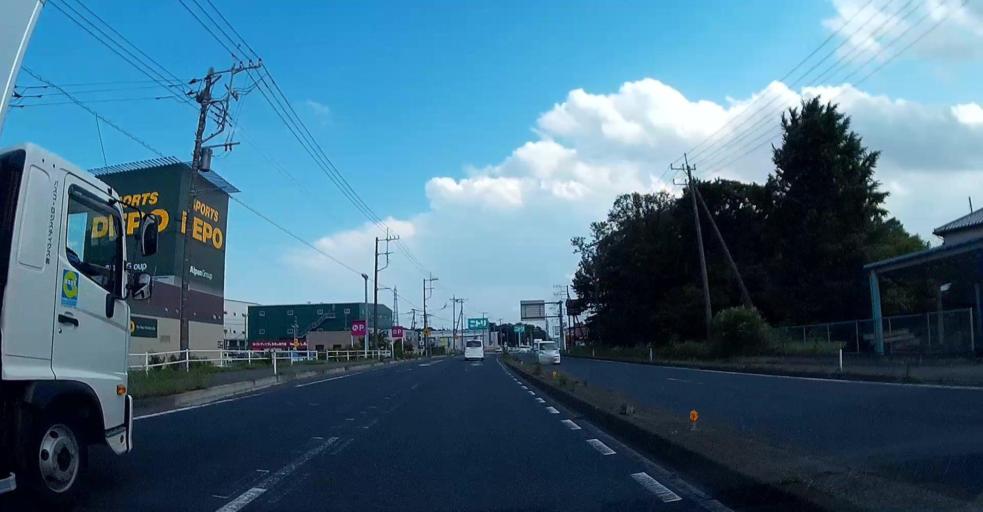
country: JP
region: Chiba
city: Noda
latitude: 35.9808
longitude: 139.8614
